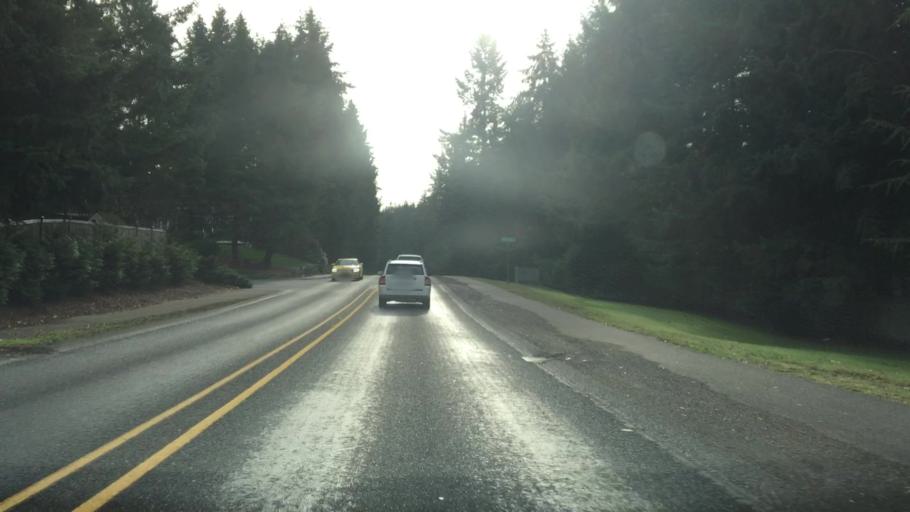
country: US
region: Washington
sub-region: Pierce County
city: South Hill
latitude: 47.1091
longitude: -122.3083
